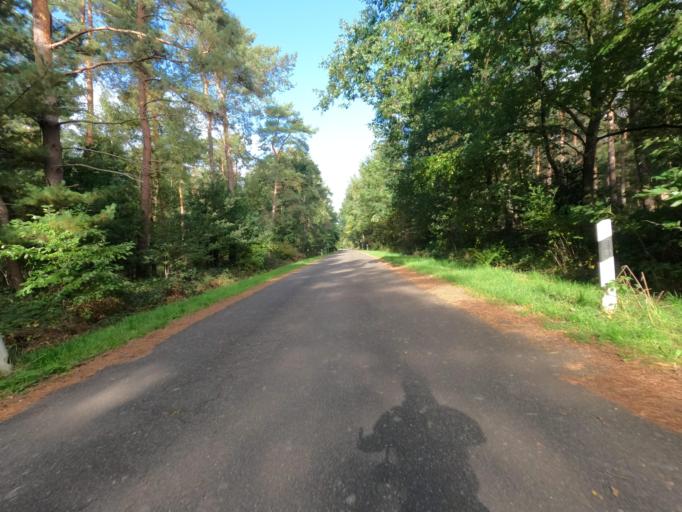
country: DE
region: North Rhine-Westphalia
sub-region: Regierungsbezirk Koln
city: Gangelt
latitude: 50.9762
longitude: 6.0520
